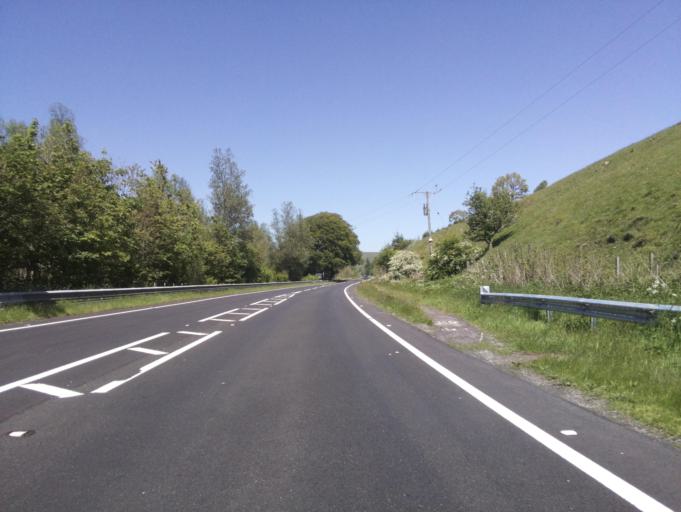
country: GB
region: Scotland
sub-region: The Scottish Borders
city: Hawick
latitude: 55.3288
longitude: -2.9429
